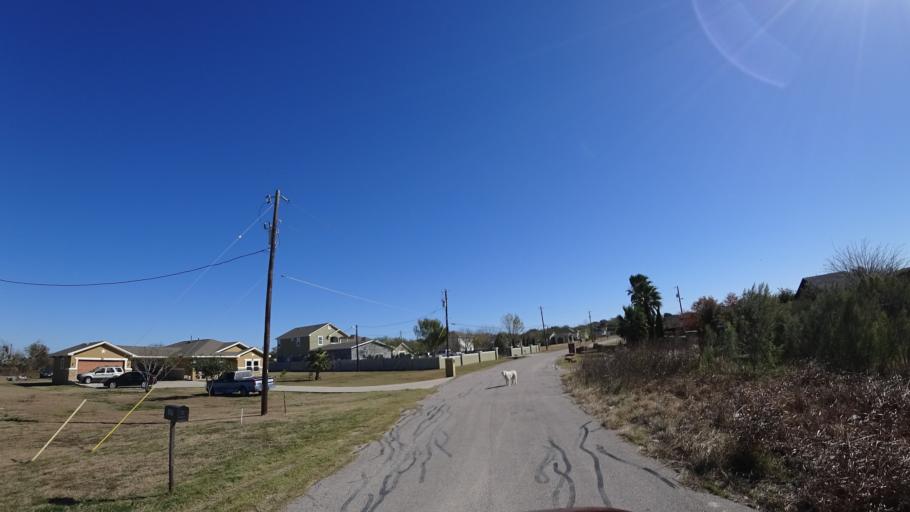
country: US
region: Texas
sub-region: Travis County
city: Garfield
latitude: 30.1086
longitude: -97.6004
